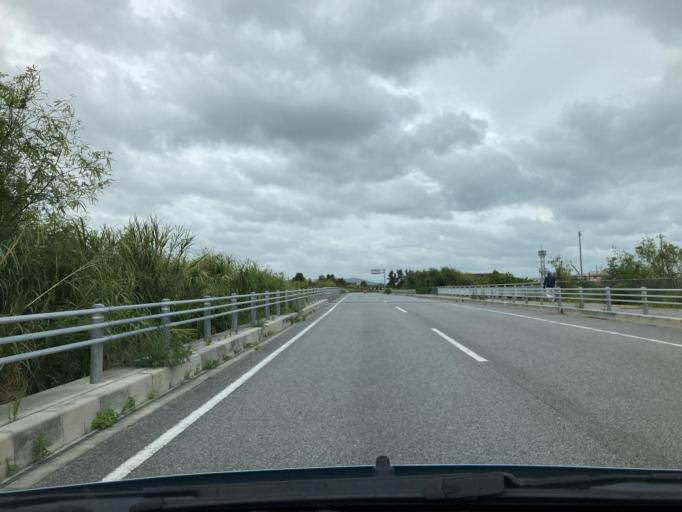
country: JP
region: Okinawa
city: Ginowan
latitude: 26.2157
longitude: 127.7721
